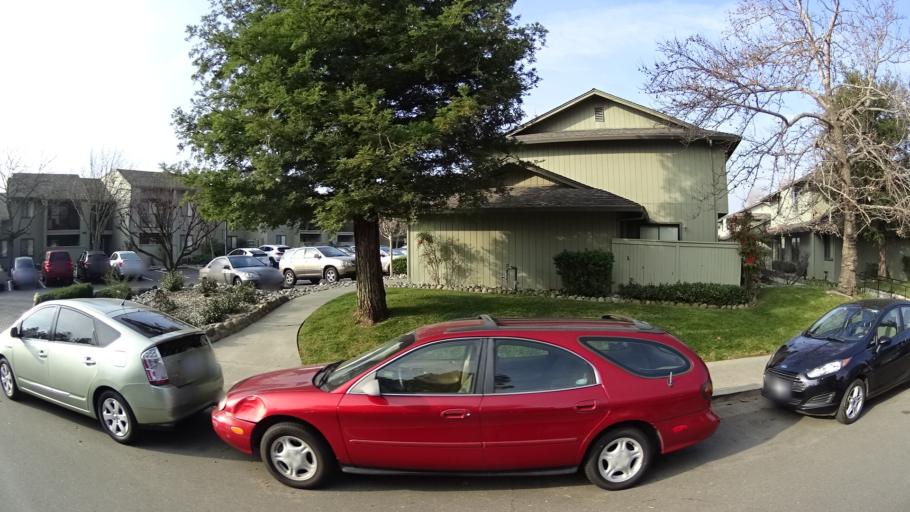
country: US
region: California
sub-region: Yolo County
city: Davis
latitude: 38.5632
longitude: -121.7657
